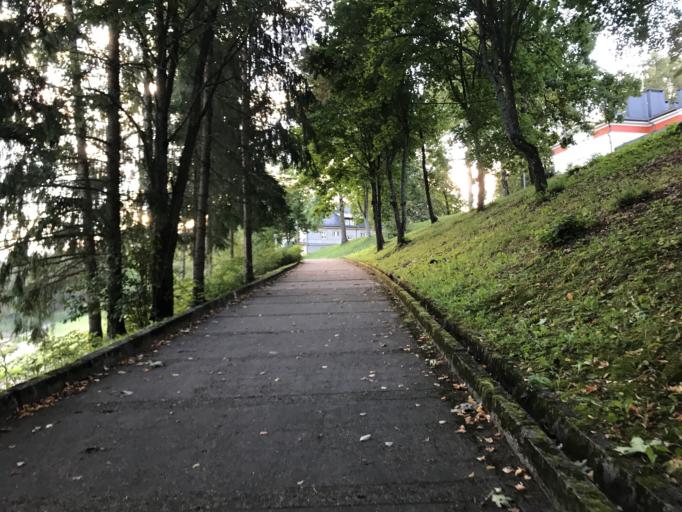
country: LT
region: Alytaus apskritis
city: Druskininkai
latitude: 54.0187
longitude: 23.9829
